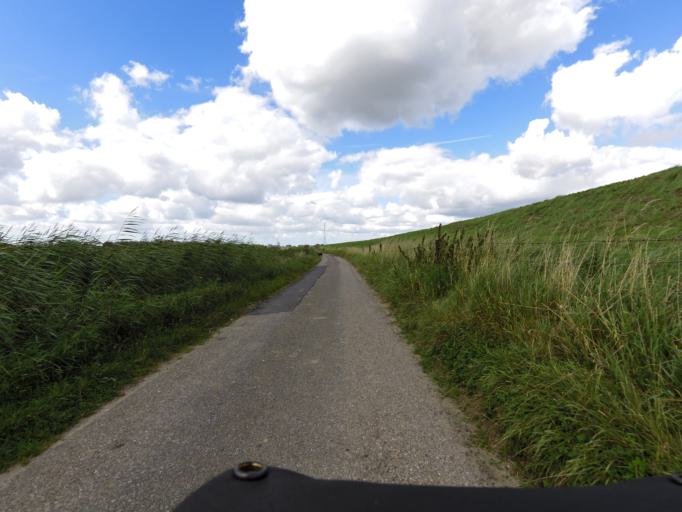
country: NL
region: South Holland
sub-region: Gemeente Oud-Beijerland
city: Oud-Beijerland
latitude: 51.8280
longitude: 4.3839
